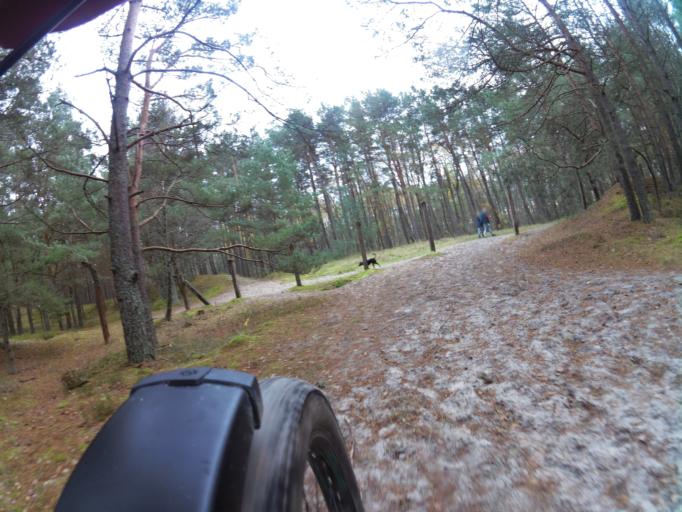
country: PL
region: Pomeranian Voivodeship
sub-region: Powiat leborski
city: Leba
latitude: 54.7677
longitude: 17.5988
